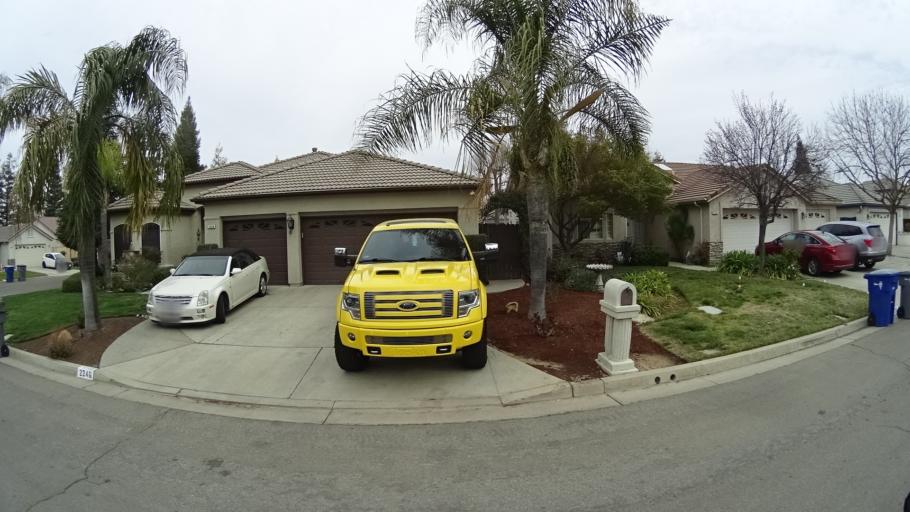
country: US
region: California
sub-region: Fresno County
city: Clovis
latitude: 36.8540
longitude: -119.7426
